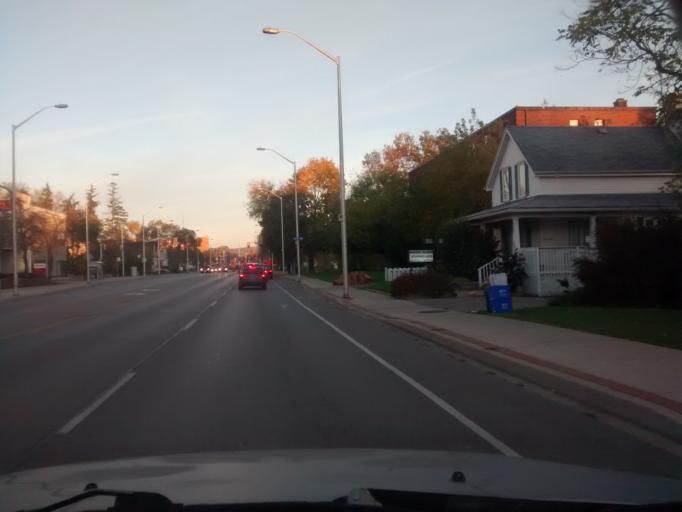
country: CA
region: Ontario
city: Burlington
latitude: 43.3325
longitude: -79.8076
